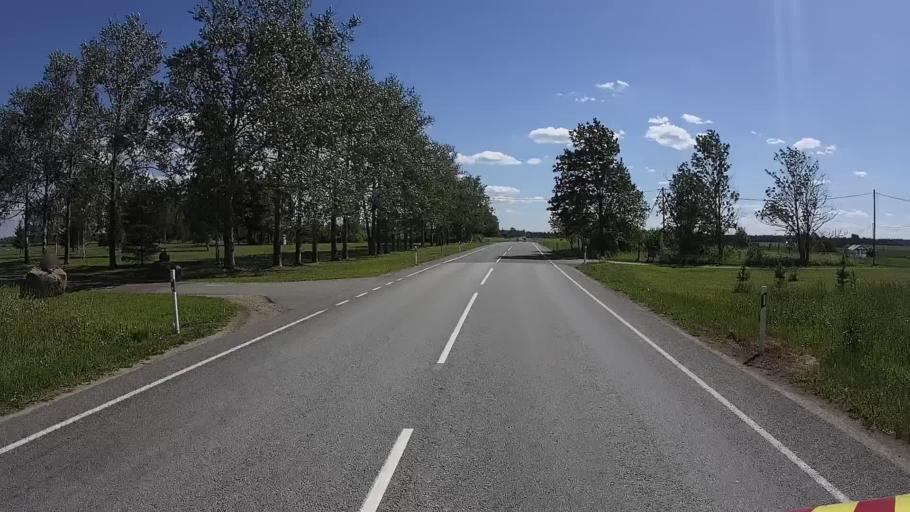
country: EE
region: Ida-Virumaa
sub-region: Johvi vald
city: Johvi
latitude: 59.3679
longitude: 27.3519
